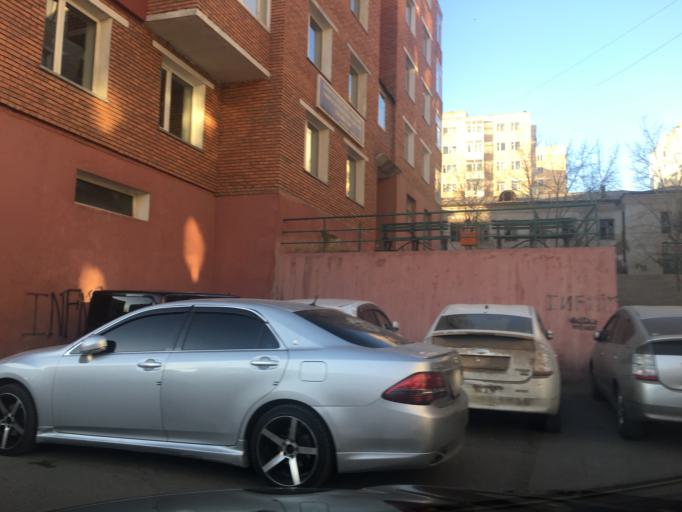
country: MN
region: Ulaanbaatar
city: Ulaanbaatar
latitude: 47.9195
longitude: 106.8831
